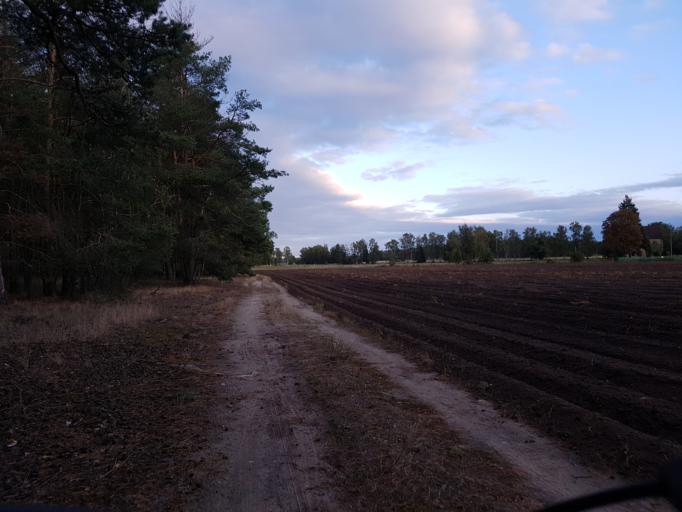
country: DE
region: Brandenburg
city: Schilda
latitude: 51.5952
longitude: 13.3628
